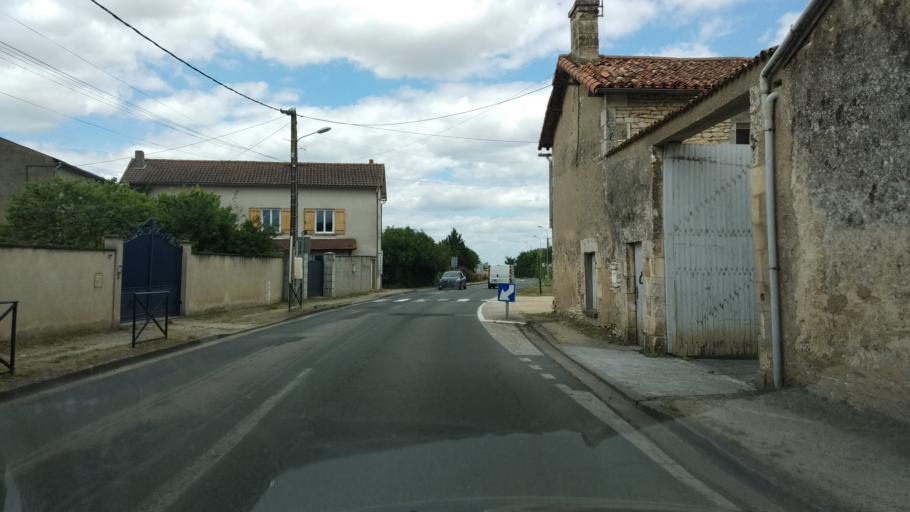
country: FR
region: Poitou-Charentes
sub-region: Departement de la Vienne
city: Avanton
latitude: 46.6643
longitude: 0.3045
